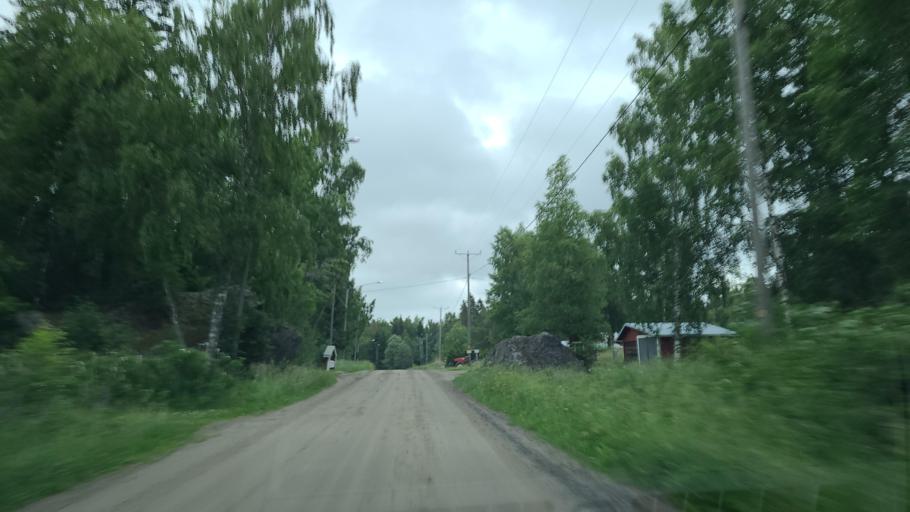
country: FI
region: Ostrobothnia
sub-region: Vaasa
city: Replot
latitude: 63.3118
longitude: 21.1593
